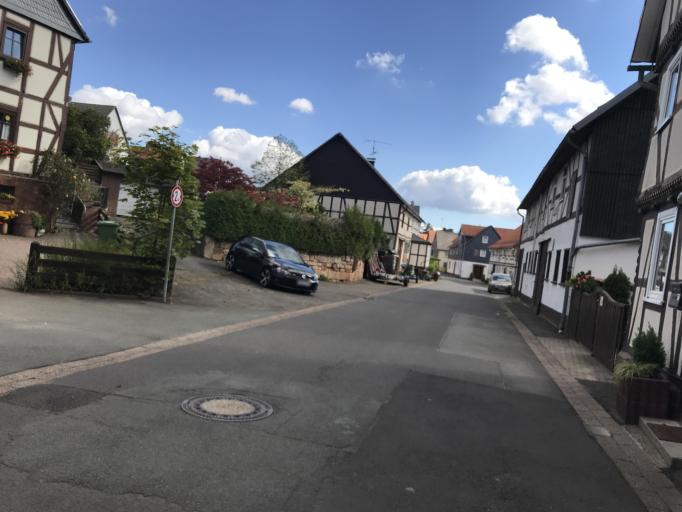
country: DE
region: Hesse
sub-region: Regierungsbezirk Kassel
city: Sachsenhausen
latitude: 51.2441
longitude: 9.0054
